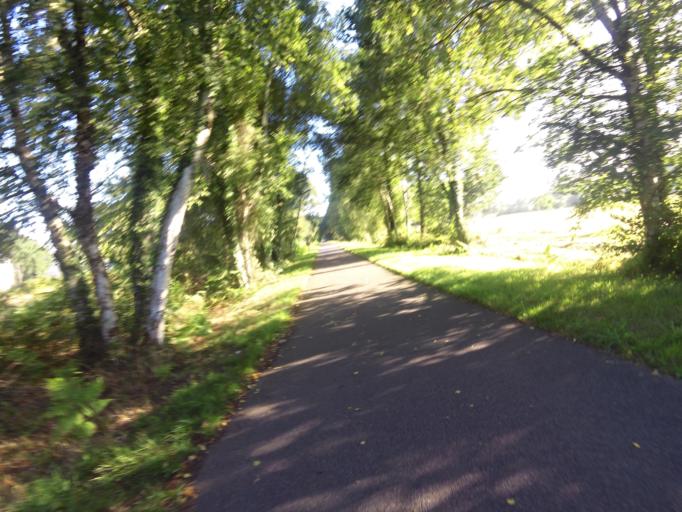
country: FR
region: Brittany
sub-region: Departement du Morbihan
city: Guillac
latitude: 47.8530
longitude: -2.4402
